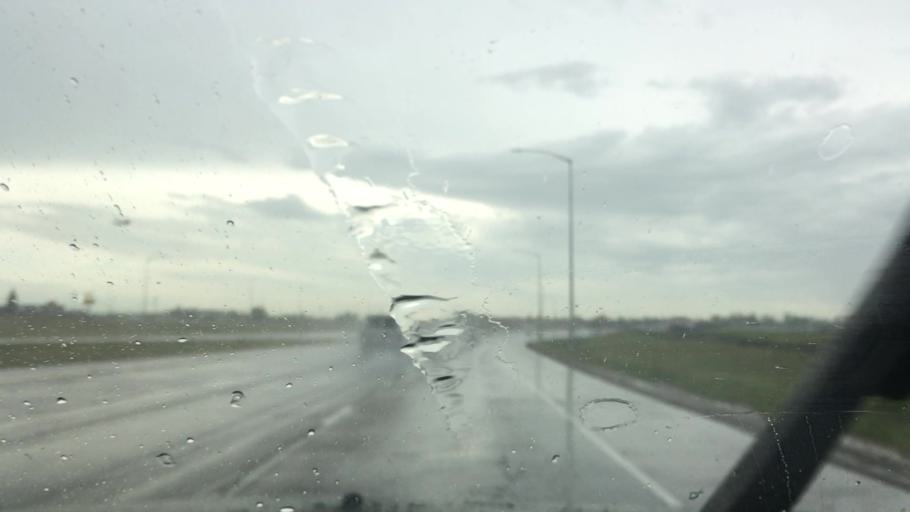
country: CA
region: Alberta
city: Leduc
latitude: 53.2843
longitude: -113.5499
